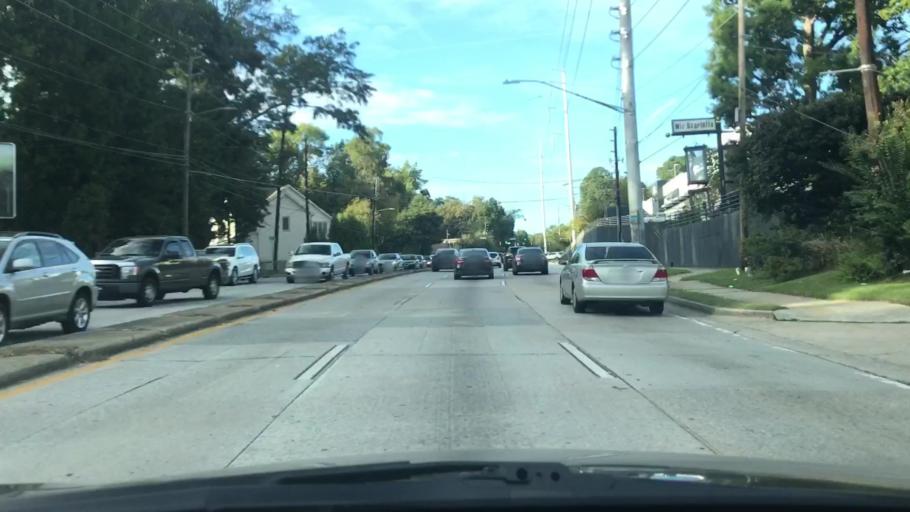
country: US
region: Georgia
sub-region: DeKalb County
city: North Atlanta
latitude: 33.8290
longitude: -84.3676
